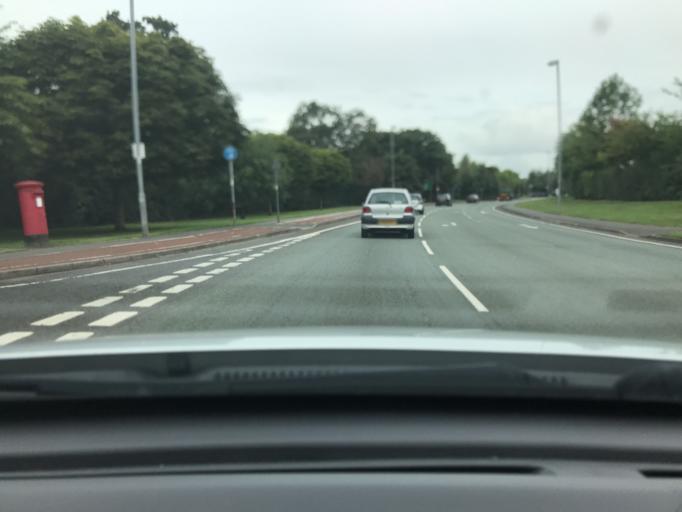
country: GB
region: England
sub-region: Cheshire West and Chester
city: Northwich
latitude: 53.2407
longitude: -2.5153
